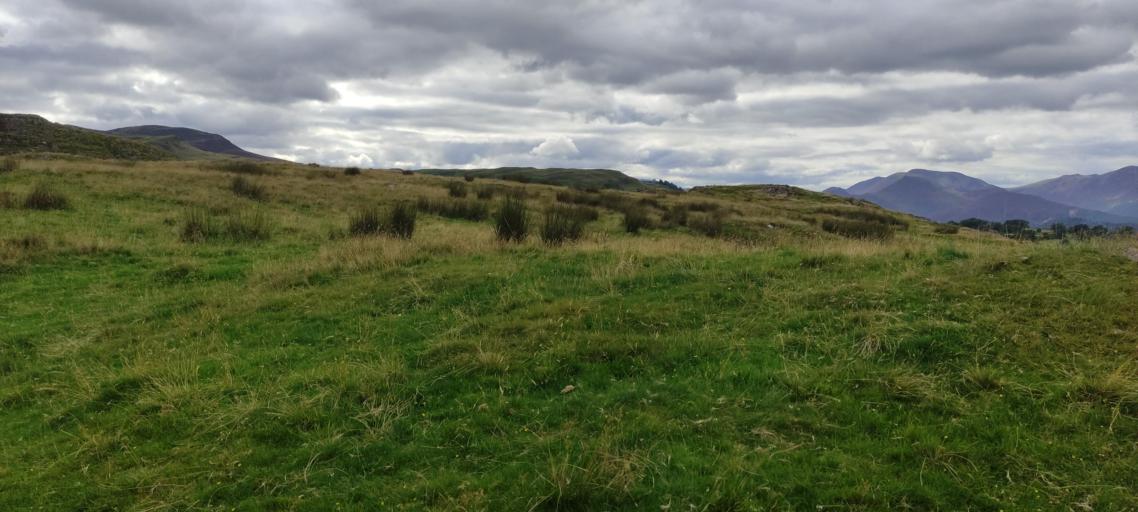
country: GB
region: England
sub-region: Cumbria
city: Keswick
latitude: 54.5974
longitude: -3.0788
